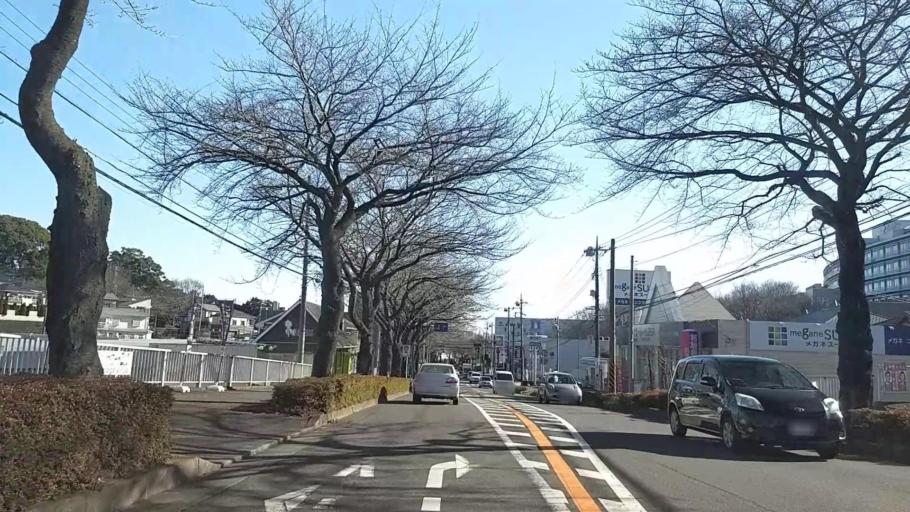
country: JP
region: Kanagawa
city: Hadano
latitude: 35.3620
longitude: 139.2277
